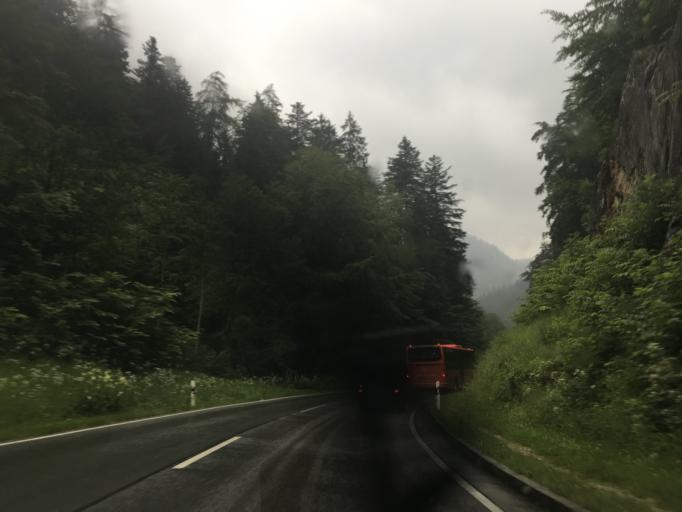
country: DE
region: Bavaria
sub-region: Upper Bavaria
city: Reit im Winkl
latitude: 47.7055
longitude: 12.4821
